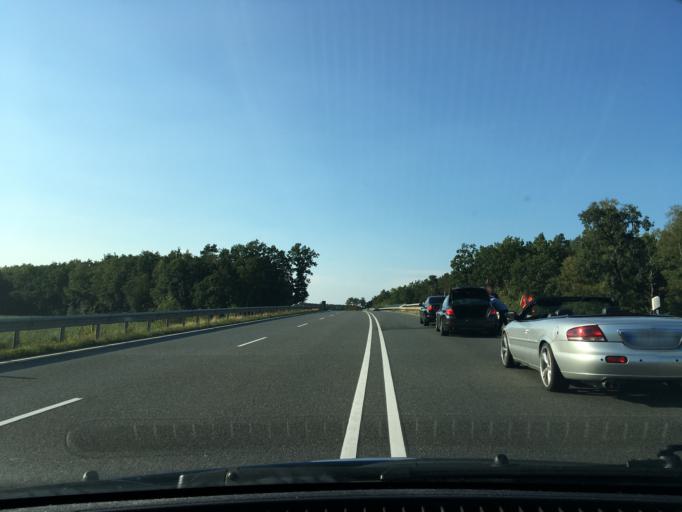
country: DE
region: Lower Saxony
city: Adelheidsdorf
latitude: 52.5753
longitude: 10.0772
